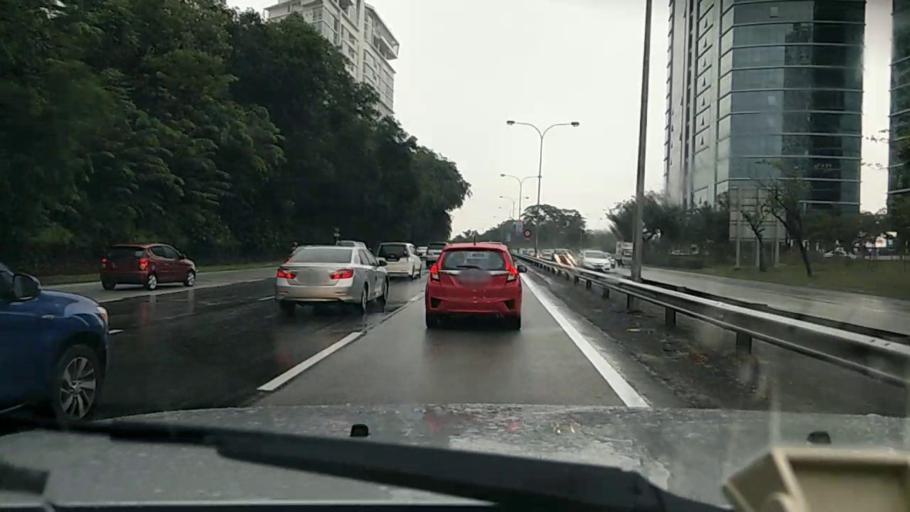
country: MY
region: Kuala Lumpur
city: Kuala Lumpur
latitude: 3.1058
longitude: 101.6934
